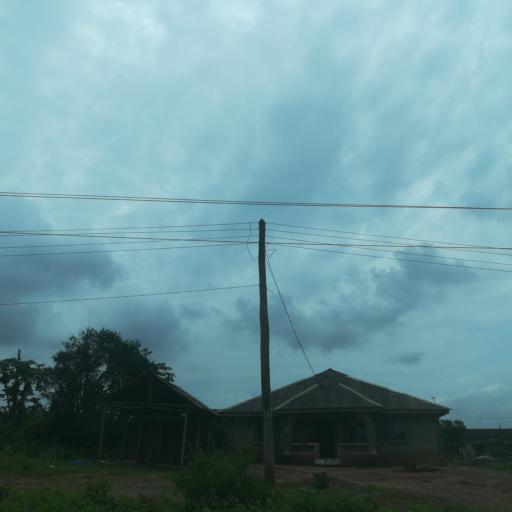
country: NG
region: Ogun
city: Odogbolu
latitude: 6.6753
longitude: 3.7124
